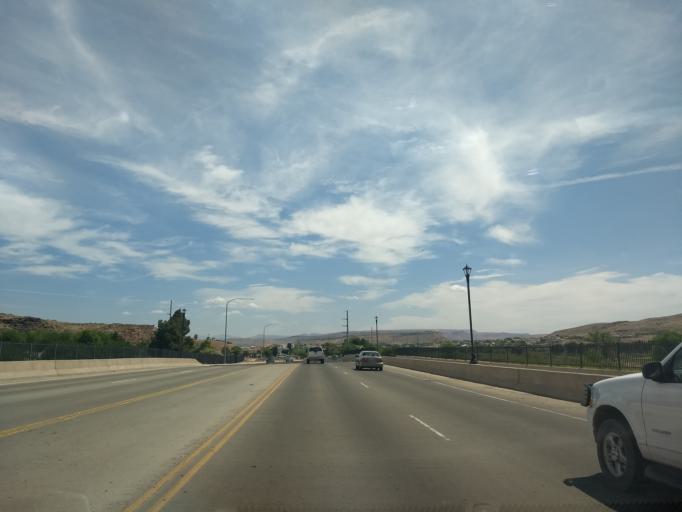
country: US
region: Utah
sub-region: Washington County
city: Saint George
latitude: 37.0764
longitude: -113.5960
